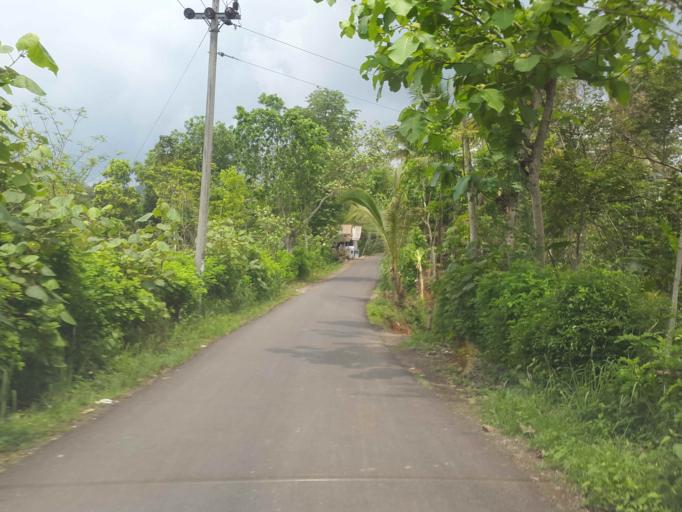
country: ID
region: Central Java
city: Pasanggrahan
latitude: -7.3693
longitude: 108.8991
